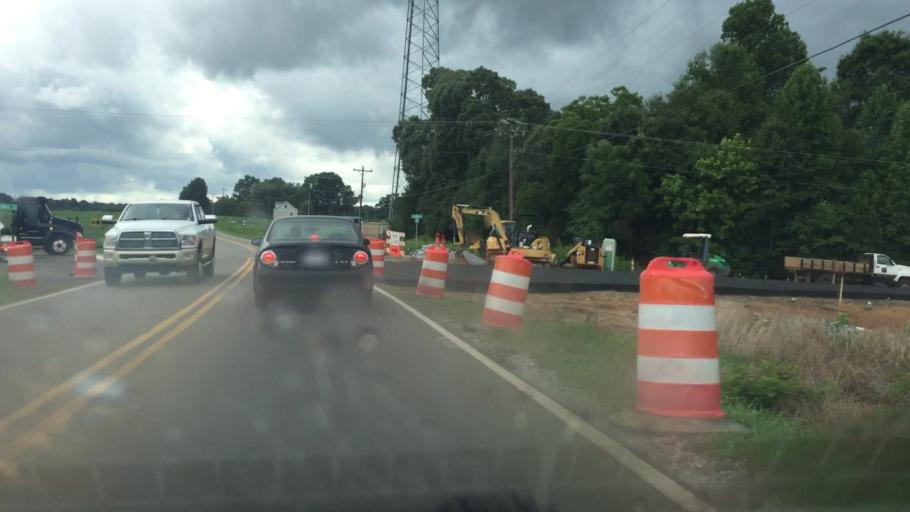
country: US
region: North Carolina
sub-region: Rowan County
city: Enochville
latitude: 35.6330
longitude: -80.6745
